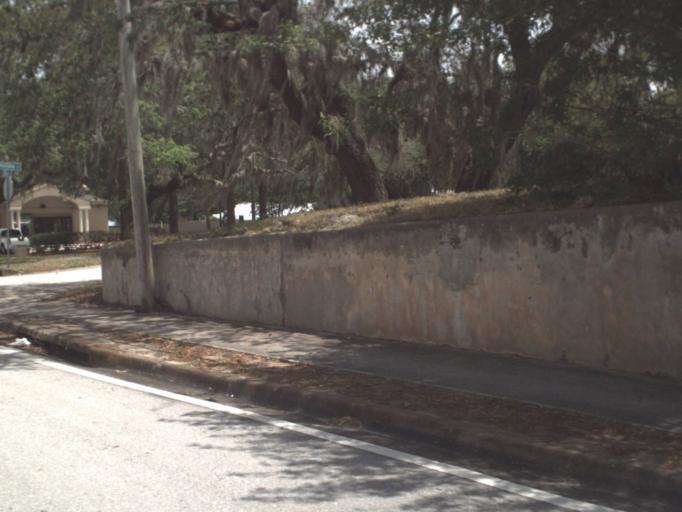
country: US
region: Florida
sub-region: Brevard County
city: Titusville
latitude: 28.6152
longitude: -80.8352
